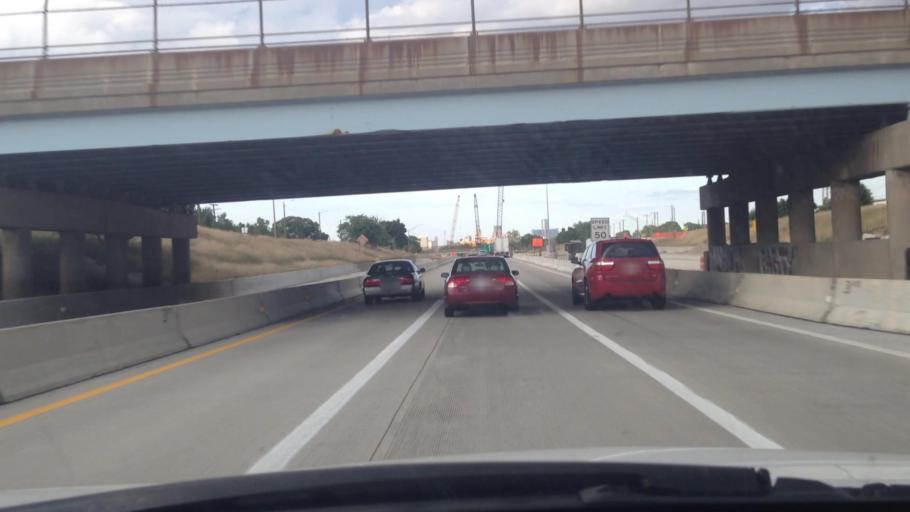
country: US
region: Michigan
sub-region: Wayne County
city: River Rouge
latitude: 42.3054
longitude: -83.1095
